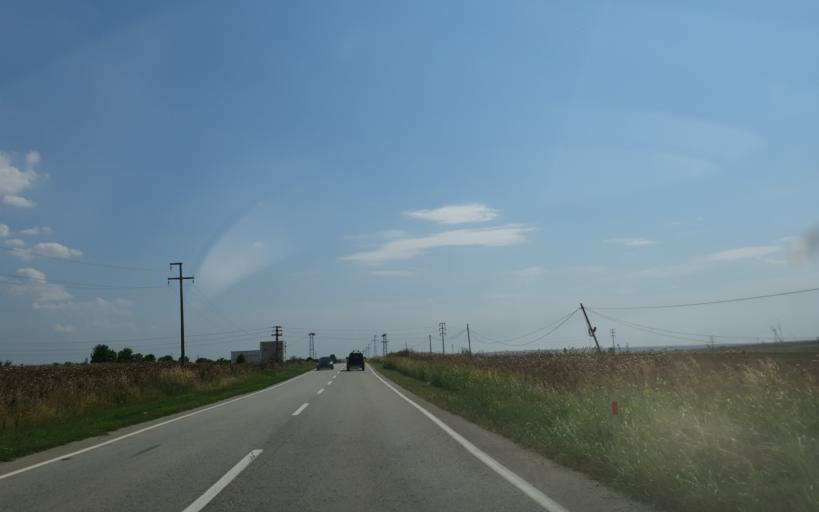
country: TR
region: Kirklareli
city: Buyukkaristiran
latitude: 41.3179
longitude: 27.5216
